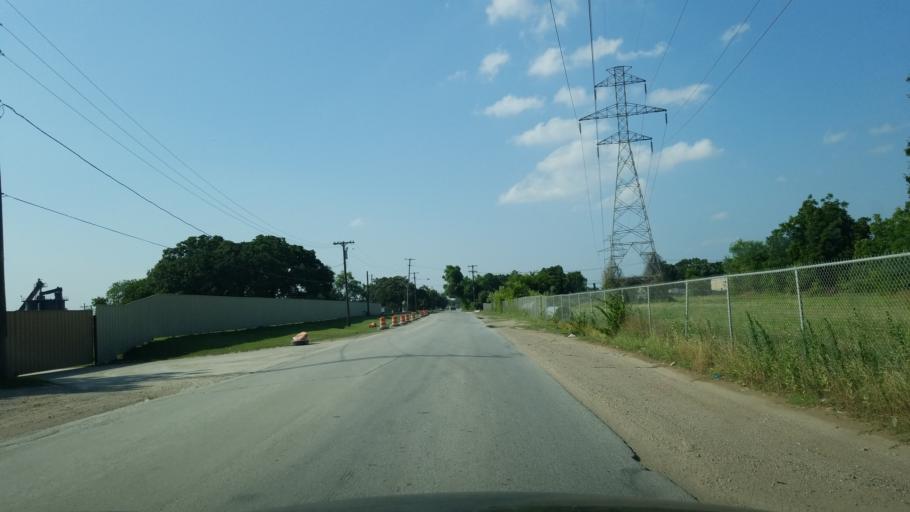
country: US
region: Texas
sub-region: Dallas County
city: Farmers Branch
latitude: 32.8847
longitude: -96.9019
